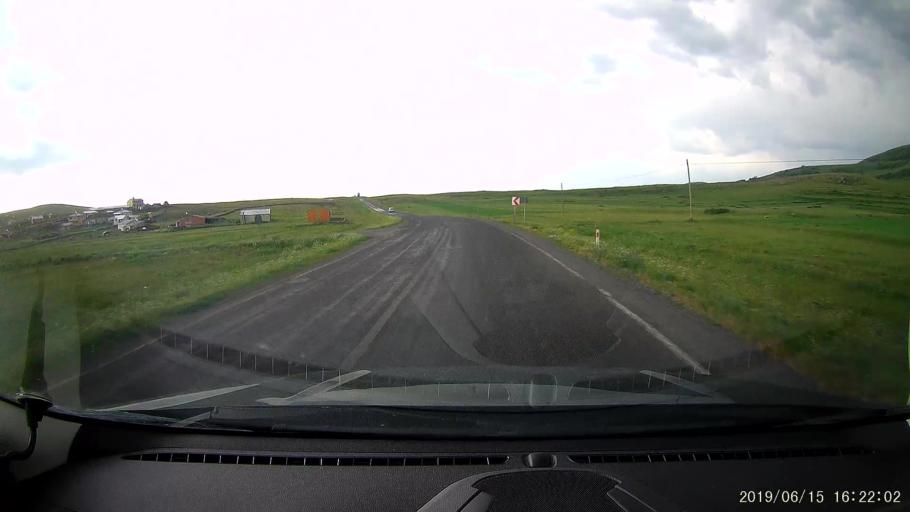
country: TR
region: Ardahan
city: Hanak
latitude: 41.1922
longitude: 42.8460
